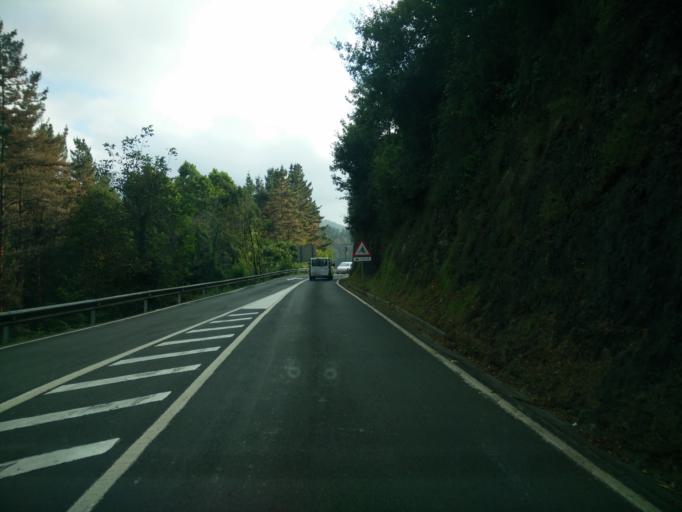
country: ES
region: Basque Country
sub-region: Bizkaia
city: Berriatua
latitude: 43.2967
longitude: -2.4755
